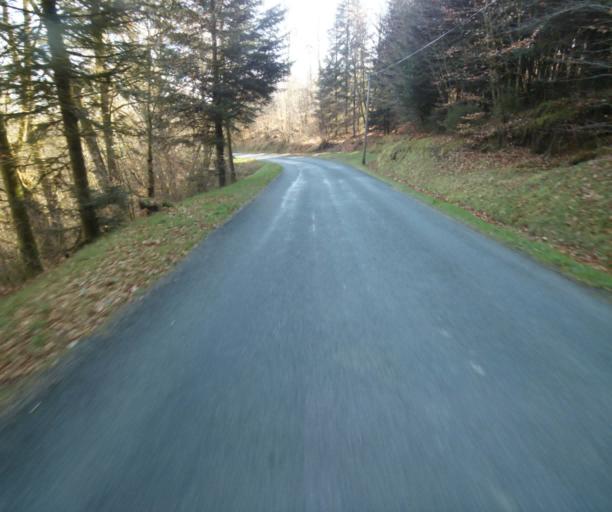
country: FR
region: Limousin
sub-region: Departement de la Correze
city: Correze
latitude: 45.3032
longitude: 1.8706
